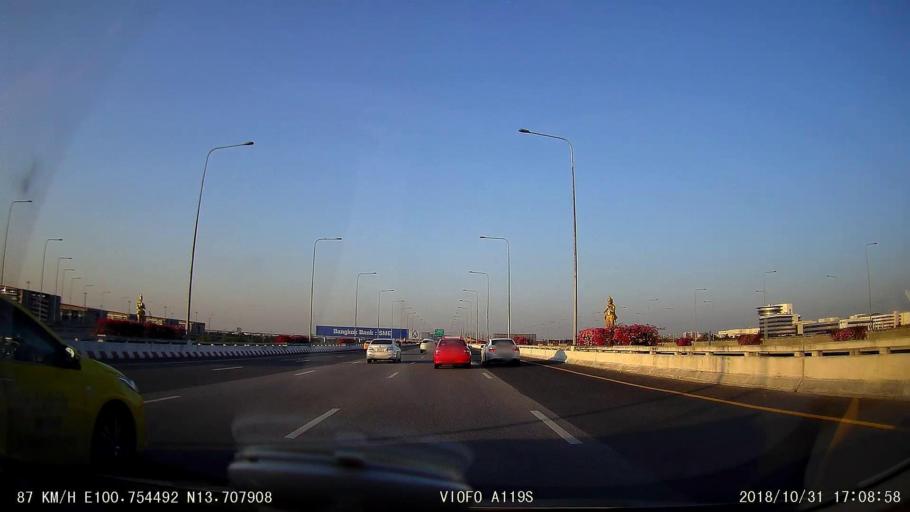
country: TH
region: Bangkok
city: Lat Krabang
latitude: 13.7080
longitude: 100.7545
